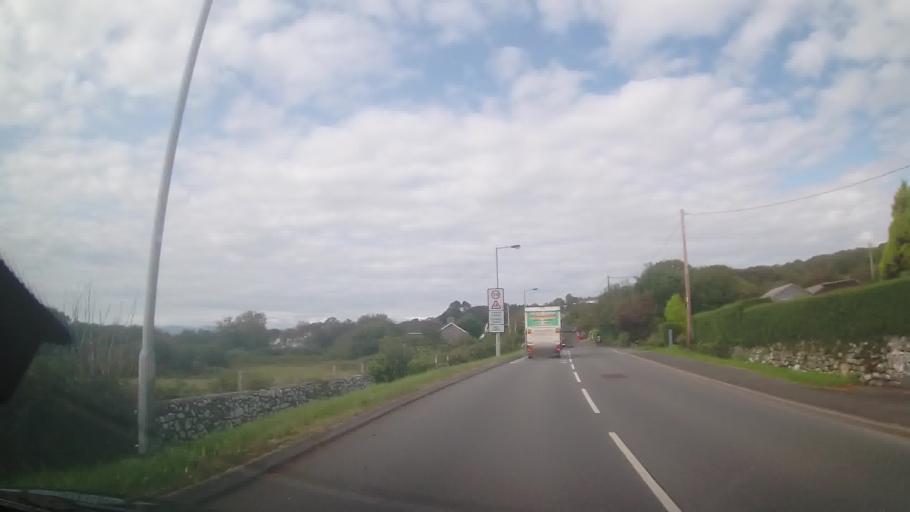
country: GB
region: Wales
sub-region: Gwynedd
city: Dyffryn Ardudwy
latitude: 52.7835
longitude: -4.0969
